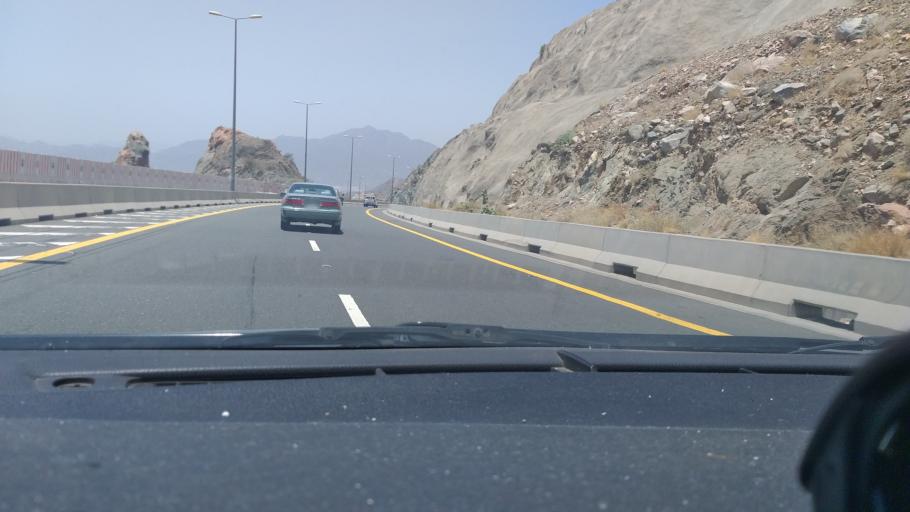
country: SA
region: Makkah
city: Al Hada
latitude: 21.3455
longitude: 40.2504
